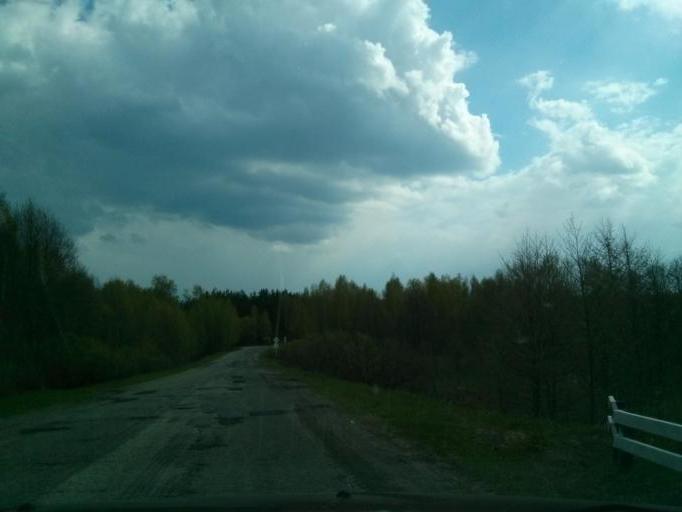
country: RU
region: Vladimir
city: Murom
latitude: 55.4574
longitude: 41.9812
